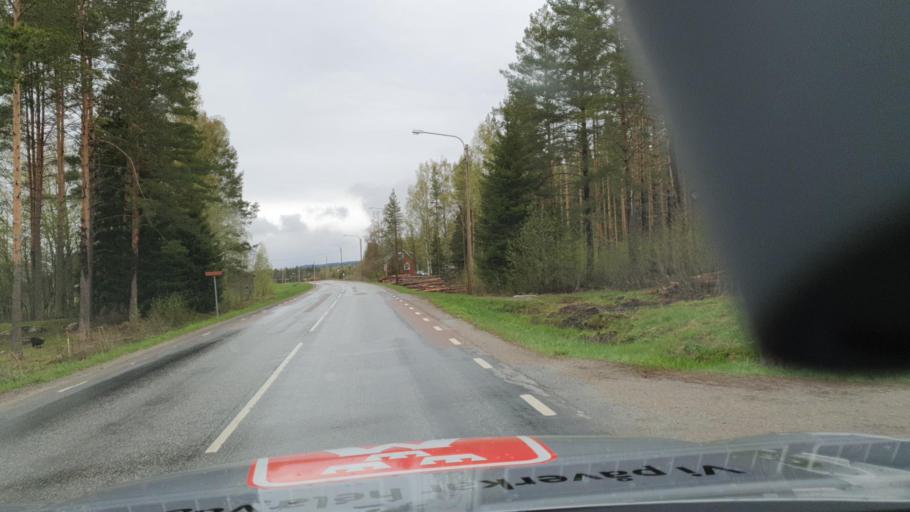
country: SE
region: Vaesternorrland
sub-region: OErnskoeldsviks Kommun
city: Bjasta
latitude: 63.3846
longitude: 18.4715
